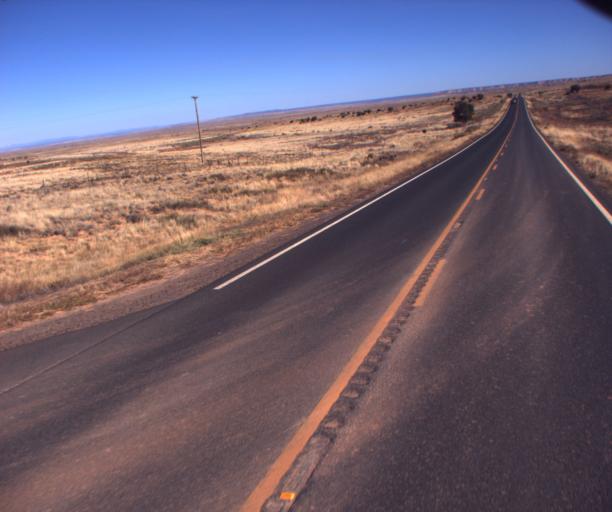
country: US
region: Arizona
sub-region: Apache County
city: Ganado
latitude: 35.7844
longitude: -109.7085
